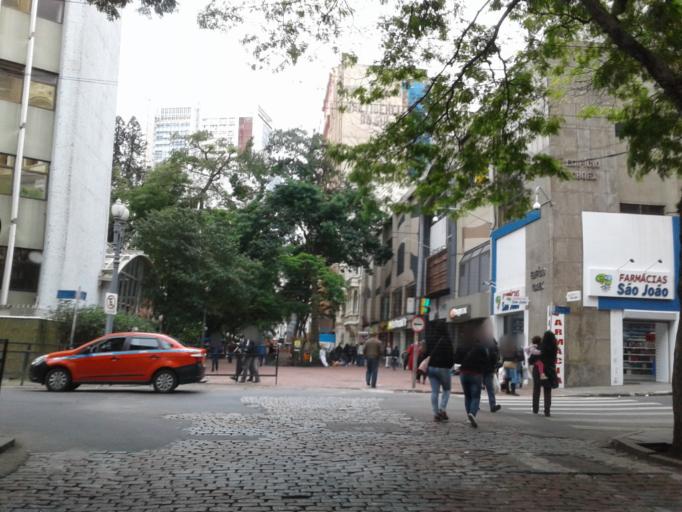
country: BR
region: Rio Grande do Sul
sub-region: Porto Alegre
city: Porto Alegre
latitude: -30.0307
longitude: -51.2320
